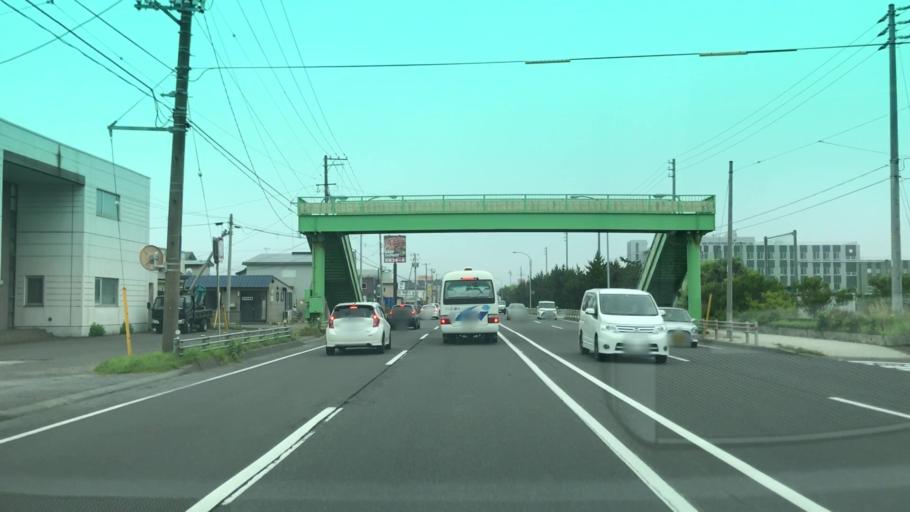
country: JP
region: Hokkaido
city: Muroran
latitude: 42.3622
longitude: 141.0555
